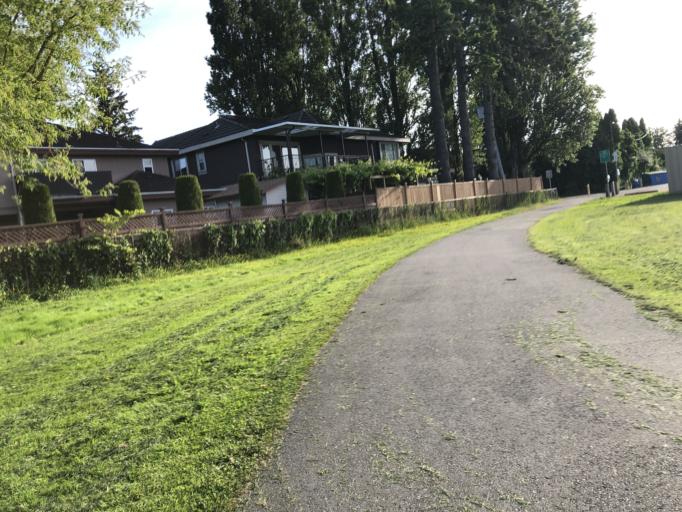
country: CA
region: British Columbia
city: Richmond
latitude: 49.1446
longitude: -123.1189
